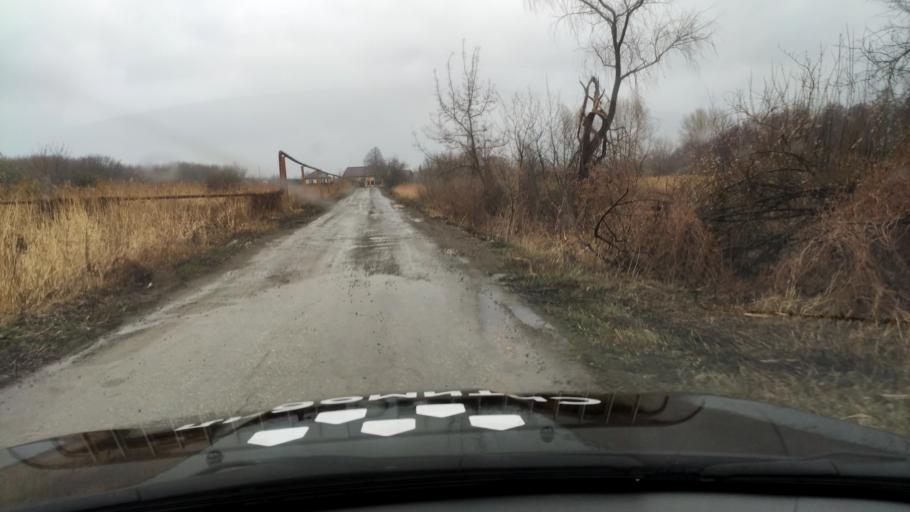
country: RU
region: Samara
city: Balasheyka
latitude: 53.2311
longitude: 48.2423
